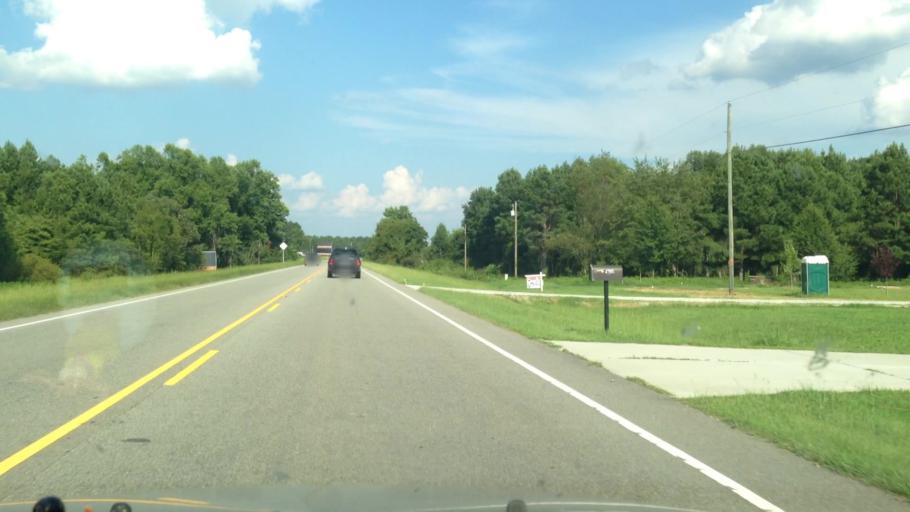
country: US
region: North Carolina
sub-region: Harnett County
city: Lillington
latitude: 35.4182
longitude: -78.8862
